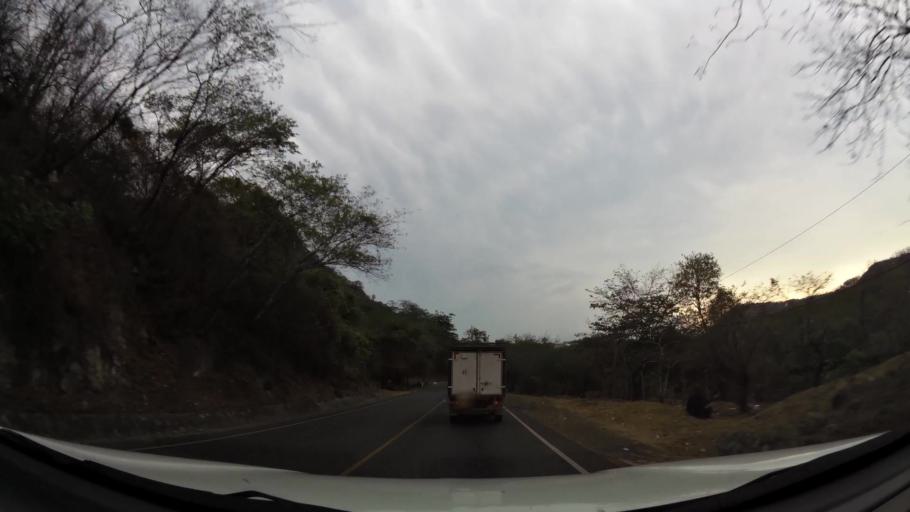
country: NI
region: Esteli
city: Esteli
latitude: 12.9474
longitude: -86.2218
